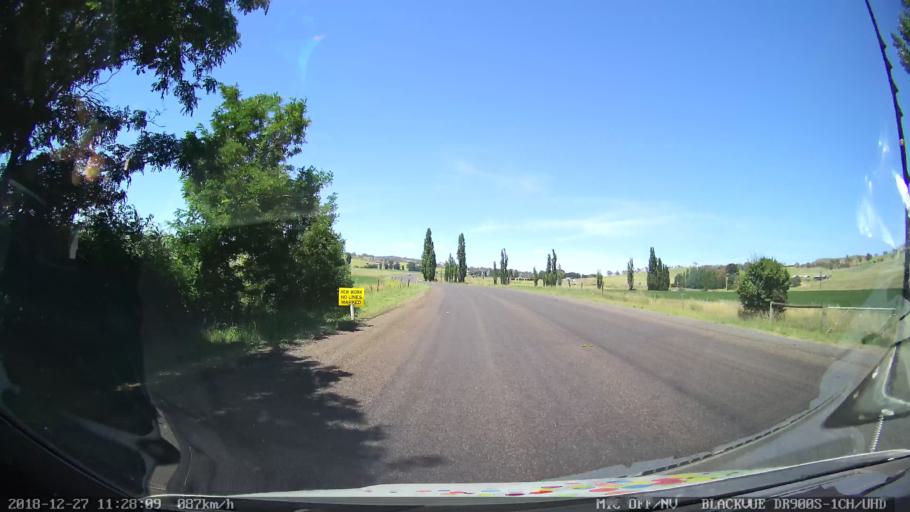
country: AU
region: New South Wales
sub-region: Bathurst Regional
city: Perthville
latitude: -33.4713
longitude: 149.5654
